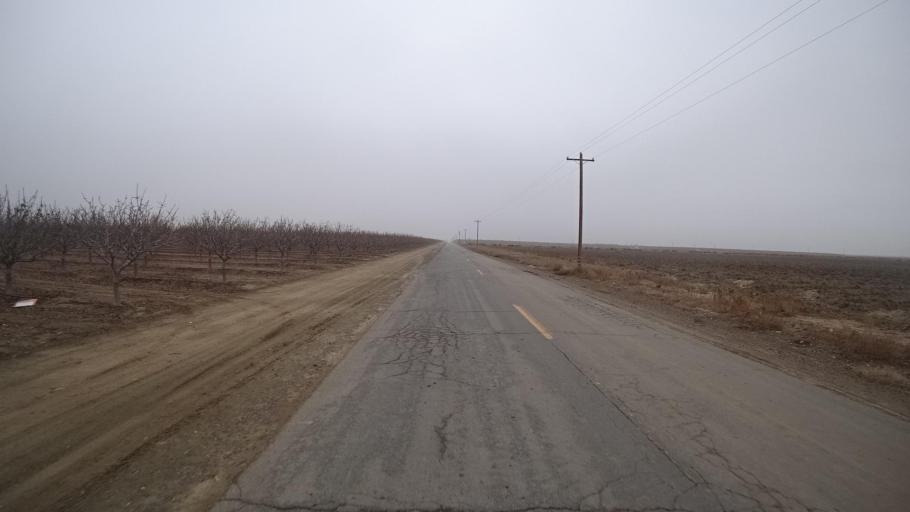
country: US
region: California
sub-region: Kern County
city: Wasco
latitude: 35.6369
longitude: -119.5088
